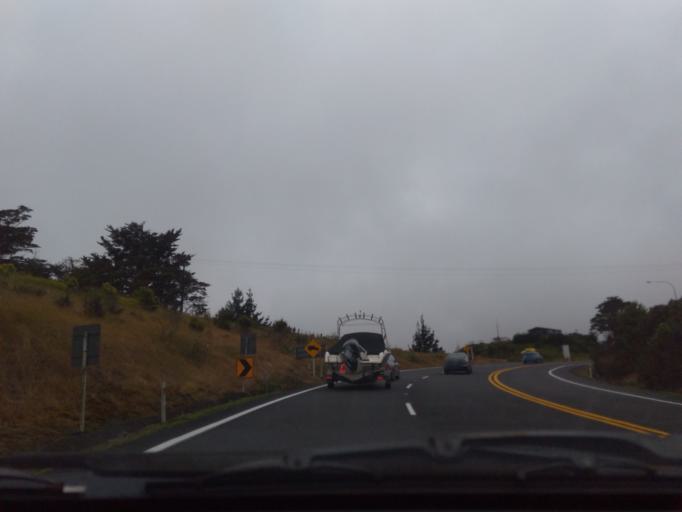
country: NZ
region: Northland
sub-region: Whangarei
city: Ruakaka
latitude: -36.0688
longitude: 174.4214
